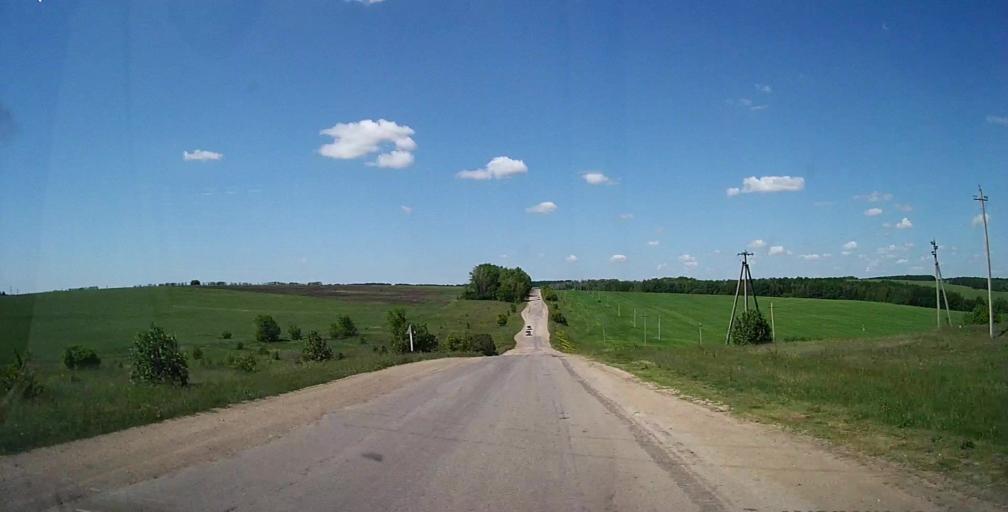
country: RU
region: Tula
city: Kurkino
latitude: 53.1888
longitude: 38.5116
